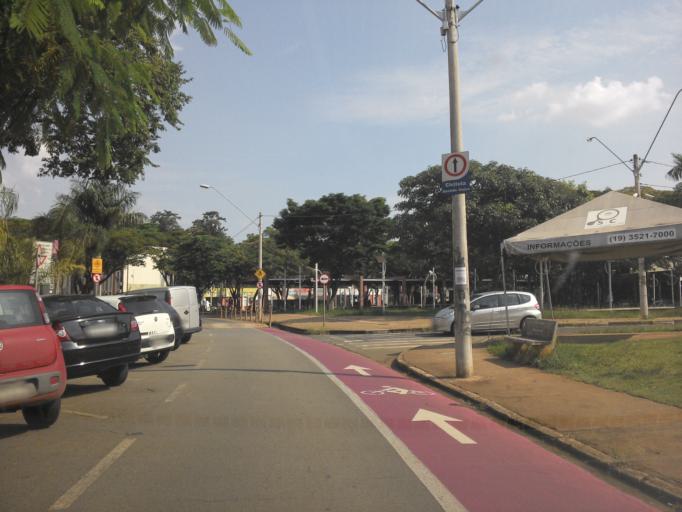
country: BR
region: Sao Paulo
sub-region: Campinas
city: Campinas
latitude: -22.8168
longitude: -47.0713
